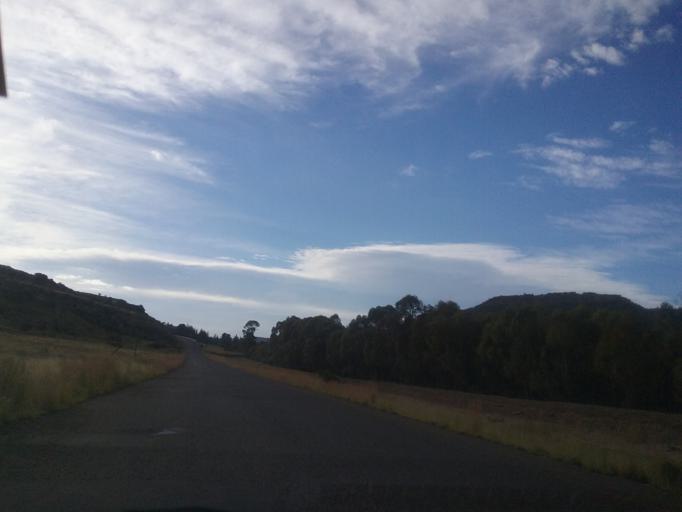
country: LS
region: Quthing
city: Quthing
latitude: -30.3883
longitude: 27.6074
